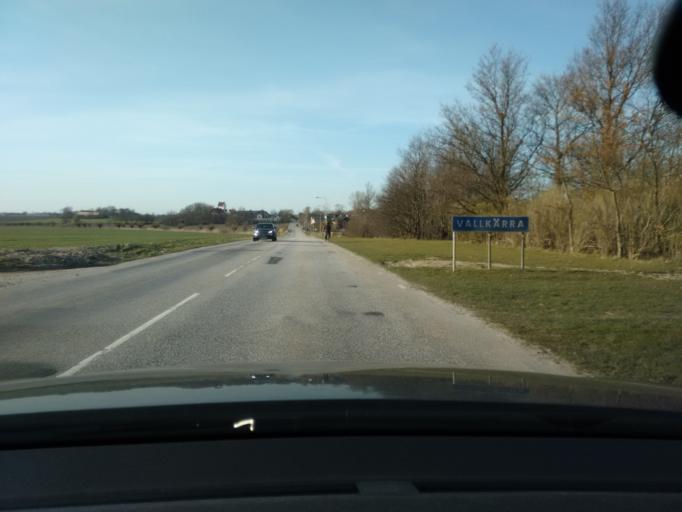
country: SE
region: Skane
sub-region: Lunds Kommun
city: Lund
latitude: 55.7365
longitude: 13.1748
